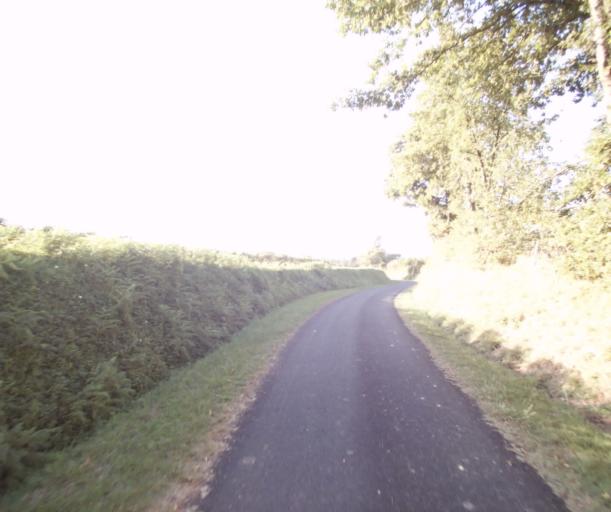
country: FR
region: Midi-Pyrenees
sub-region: Departement du Gers
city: Eauze
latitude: 43.8586
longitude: 0.0111
